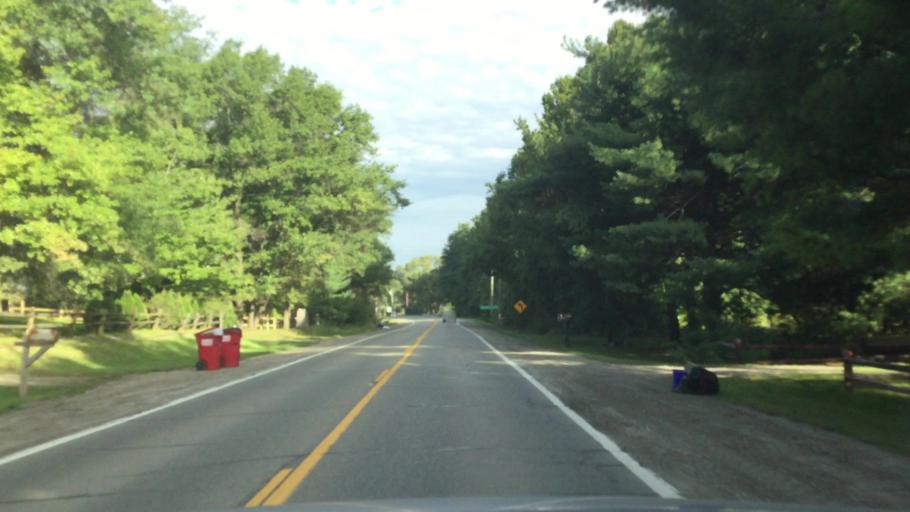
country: US
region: Michigan
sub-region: Livingston County
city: Brighton
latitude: 42.5244
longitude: -83.8588
